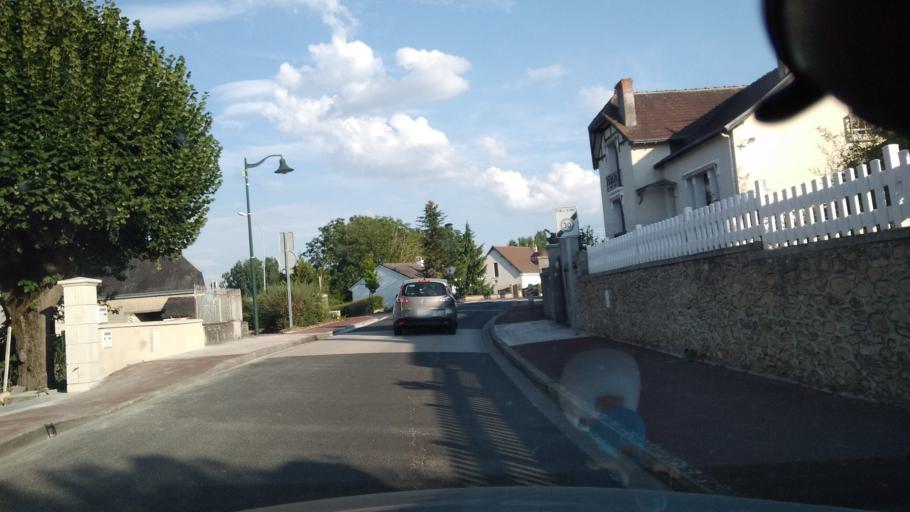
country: FR
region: Centre
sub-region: Departement d'Indre-et-Loire
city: Chambourg-sur-Indre
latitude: 47.1796
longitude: 0.9701
